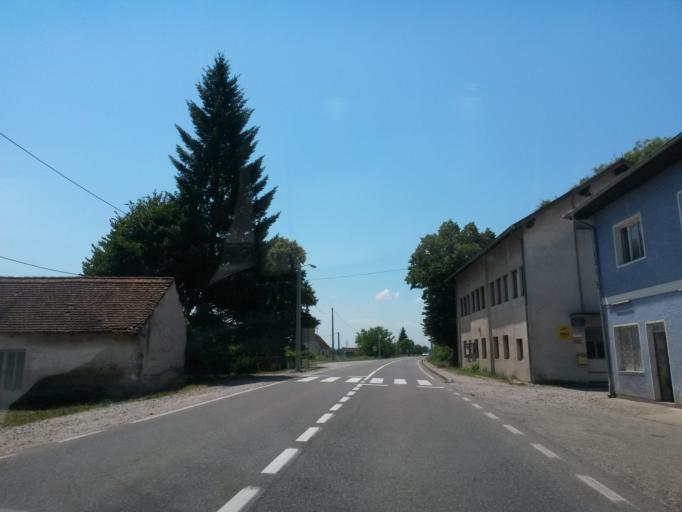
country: BA
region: Federation of Bosnia and Herzegovina
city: Lukavica
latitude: 44.8875
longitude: 18.0935
